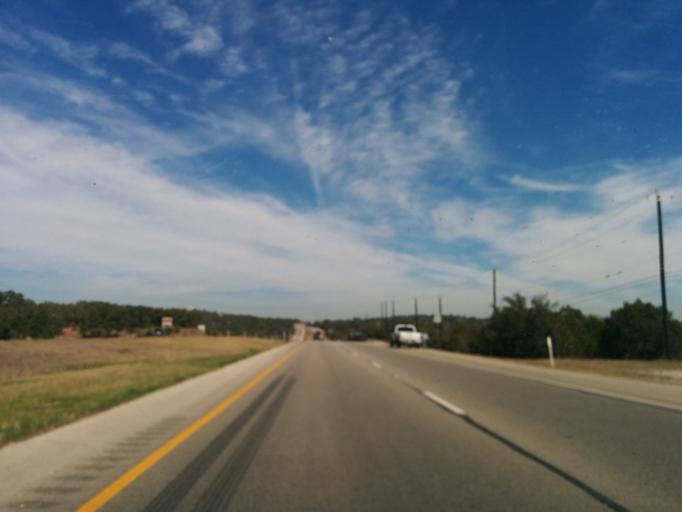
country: US
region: Texas
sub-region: Comal County
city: Bulverde
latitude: 29.7484
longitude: -98.4321
